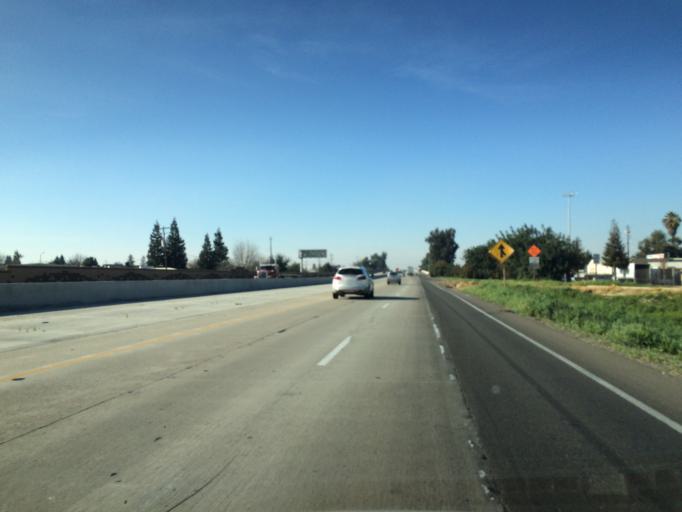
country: US
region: California
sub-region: Fresno County
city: Kingsburg
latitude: 36.5089
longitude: -119.5507
